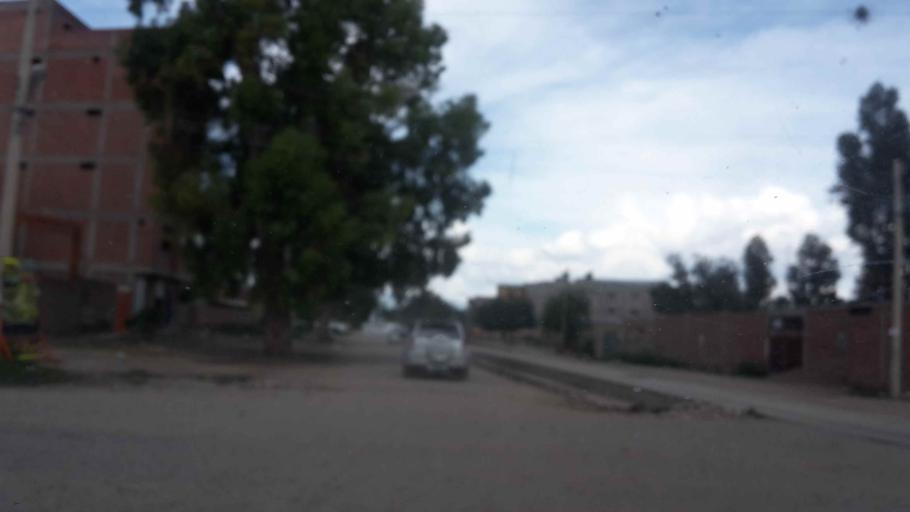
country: BO
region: Cochabamba
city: Sipe Sipe
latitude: -17.4015
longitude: -66.2765
